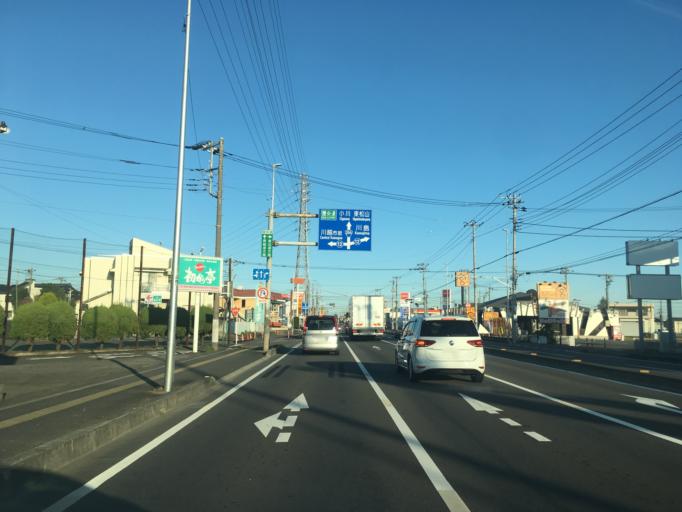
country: JP
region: Saitama
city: Kawagoe
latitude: 35.9342
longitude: 139.4870
